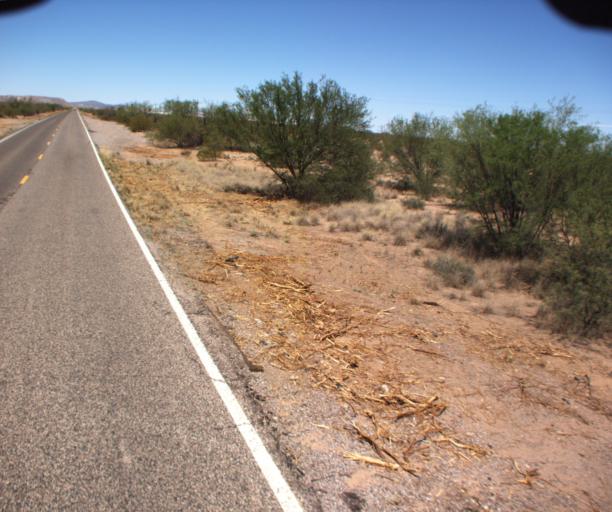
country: US
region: Arizona
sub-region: Pima County
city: Ajo
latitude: 32.3326
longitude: -112.7874
